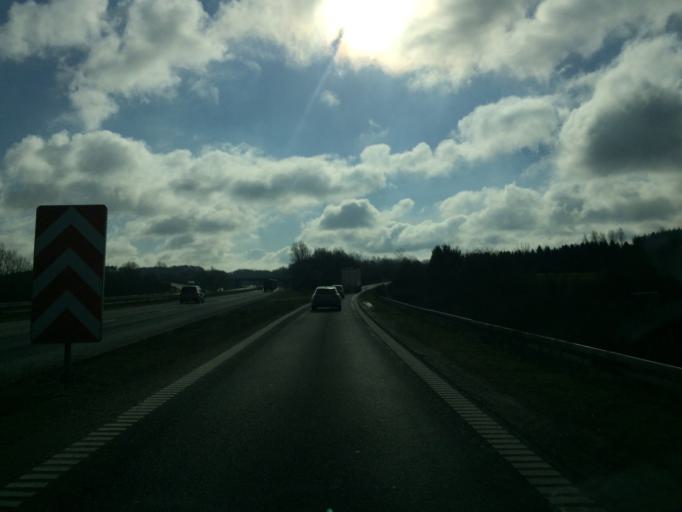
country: DK
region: South Denmark
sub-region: Assens Kommune
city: Tommerup Stationsby
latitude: 55.3896
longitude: 10.2048
